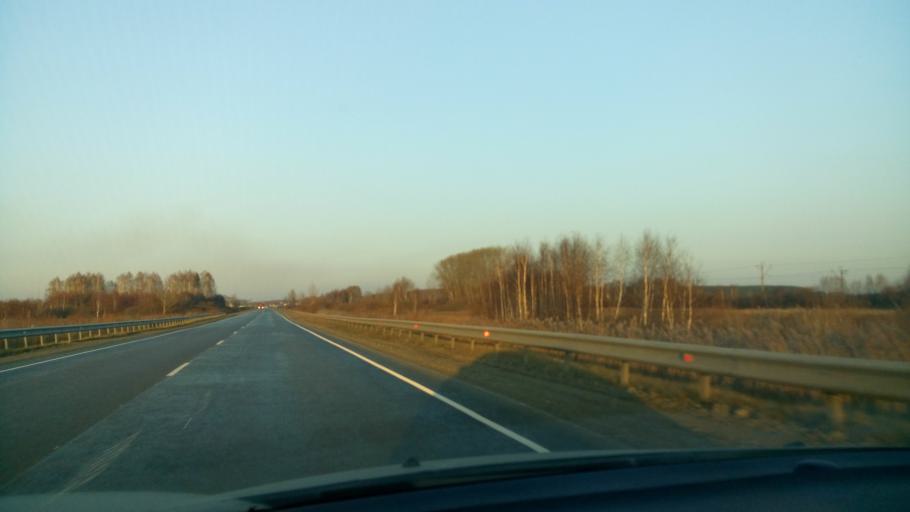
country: RU
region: Sverdlovsk
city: Obukhovskoye
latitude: 56.8312
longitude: 62.5662
